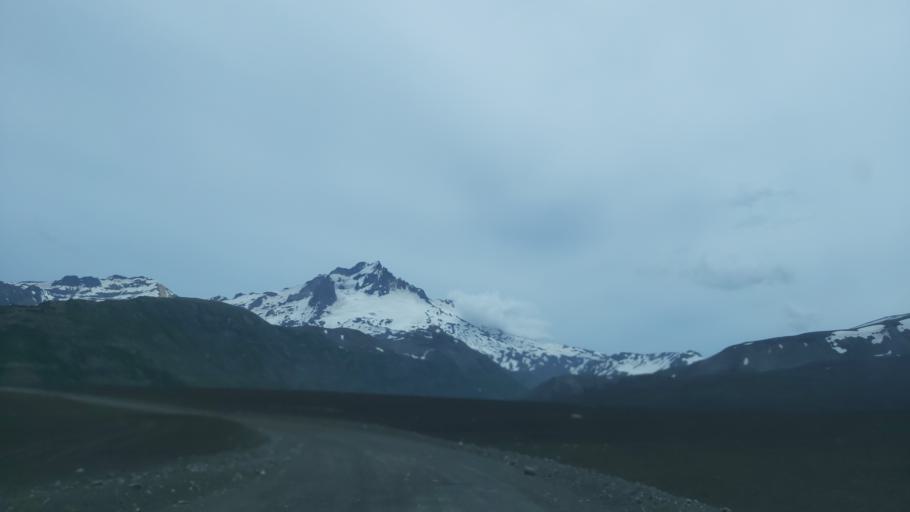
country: AR
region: Neuquen
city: Andacollo
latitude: -37.4584
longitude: -71.3024
